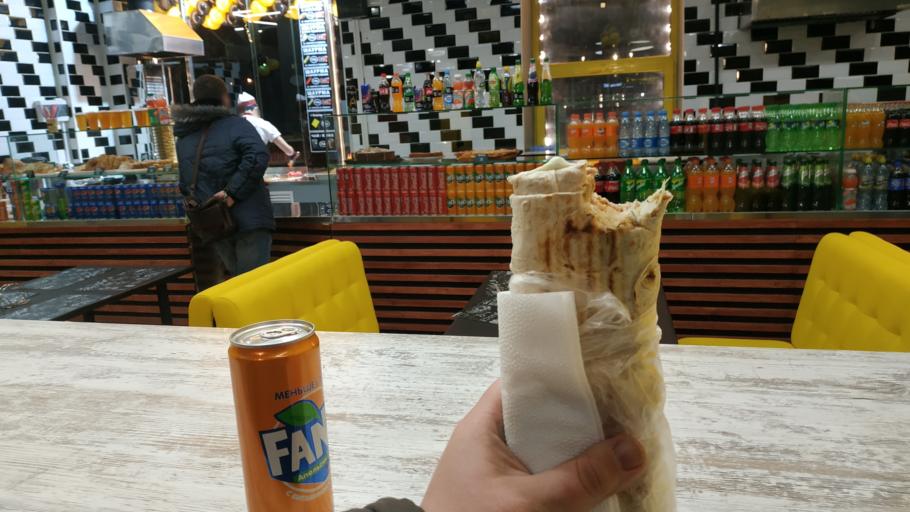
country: RU
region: Moscow
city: Novovladykino
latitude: 55.8442
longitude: 37.5763
